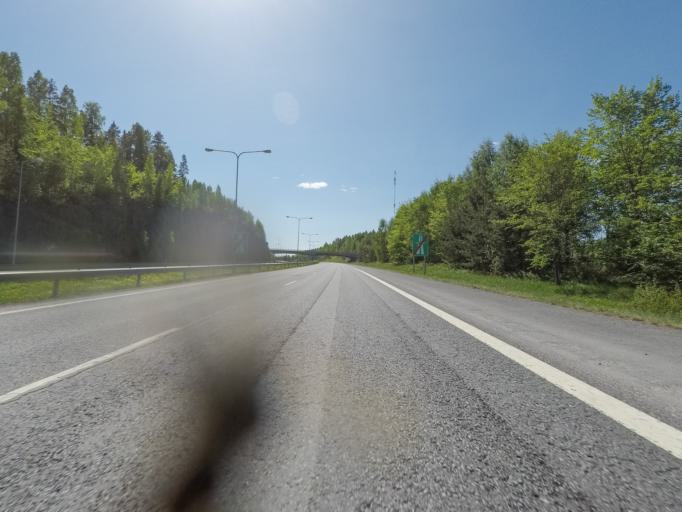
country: FI
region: Pirkanmaa
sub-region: Etelae-Pirkanmaa
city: Toijala
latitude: 61.1981
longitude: 23.8201
